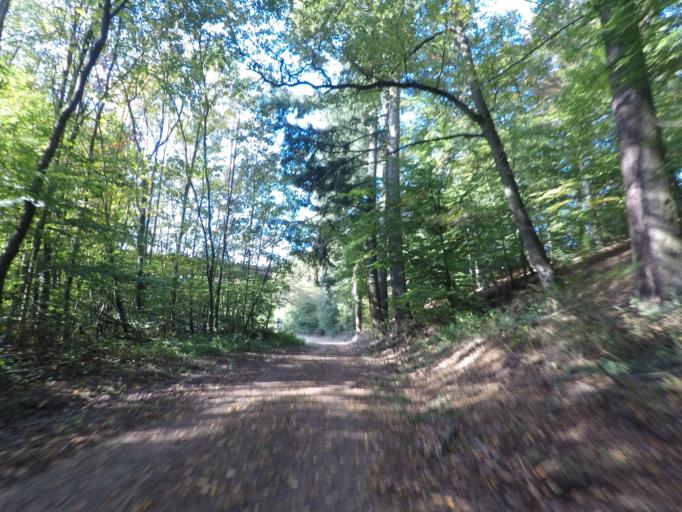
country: LU
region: Luxembourg
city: Itzig
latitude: 49.5956
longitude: 6.1727
